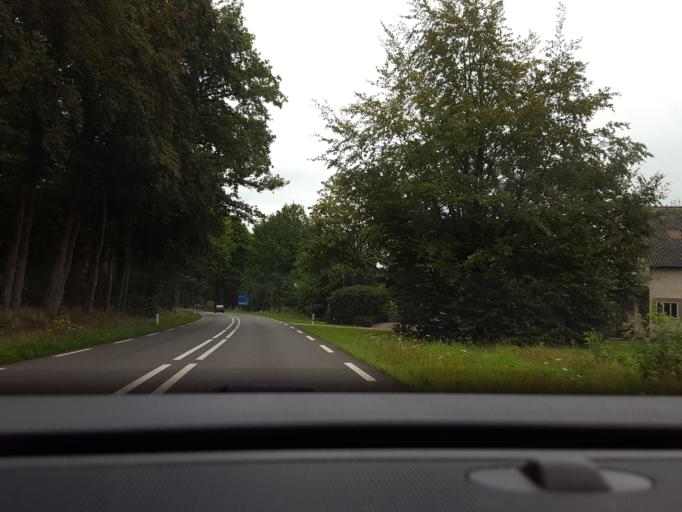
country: NL
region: Gelderland
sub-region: Gemeente Brummen
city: Brummen
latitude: 52.0892
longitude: 6.1364
